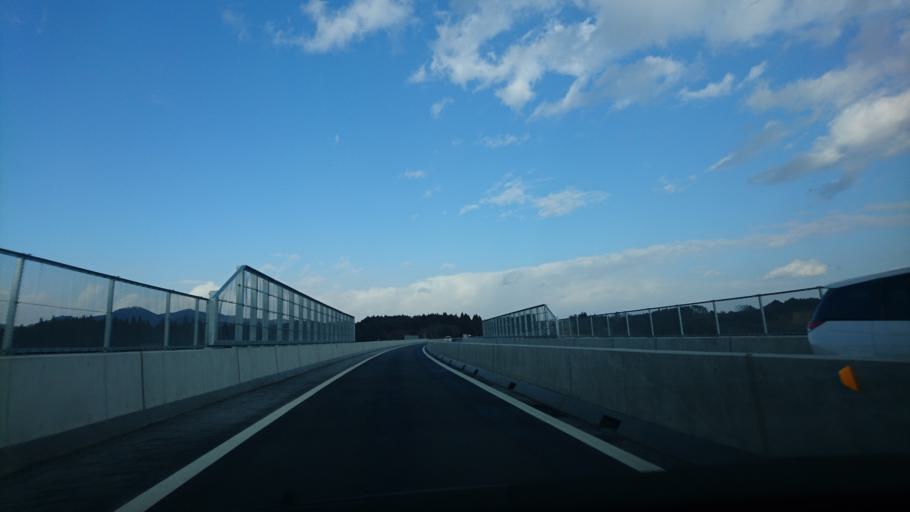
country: JP
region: Miyagi
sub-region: Oshika Gun
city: Onagawa Cho
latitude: 38.7737
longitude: 141.4986
